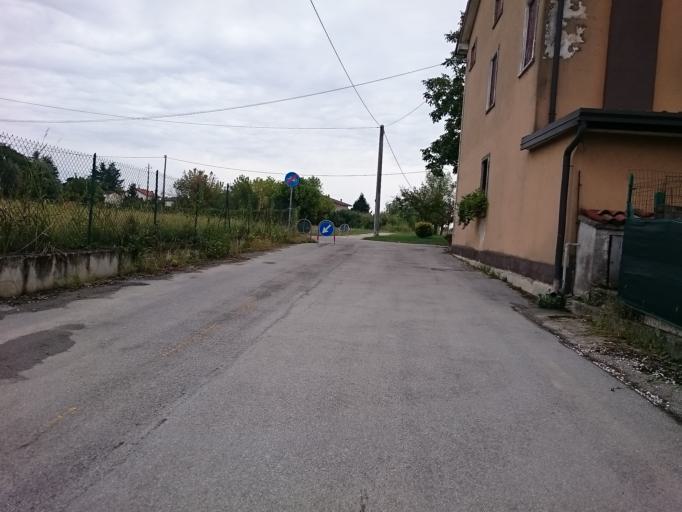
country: IT
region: Veneto
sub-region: Provincia di Vicenza
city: Quinto Vicentino
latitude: 45.5637
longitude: 11.6447
